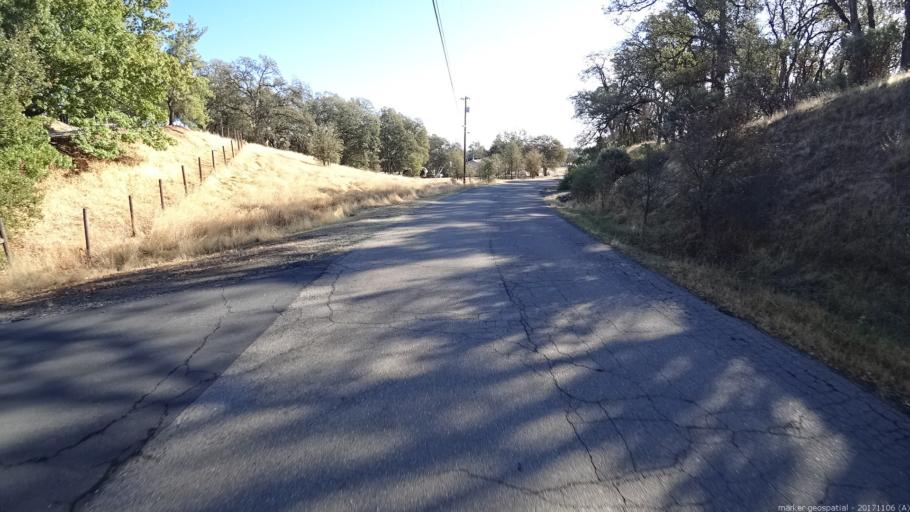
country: US
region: California
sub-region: Shasta County
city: Palo Cedro
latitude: 40.5117
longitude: -122.2414
